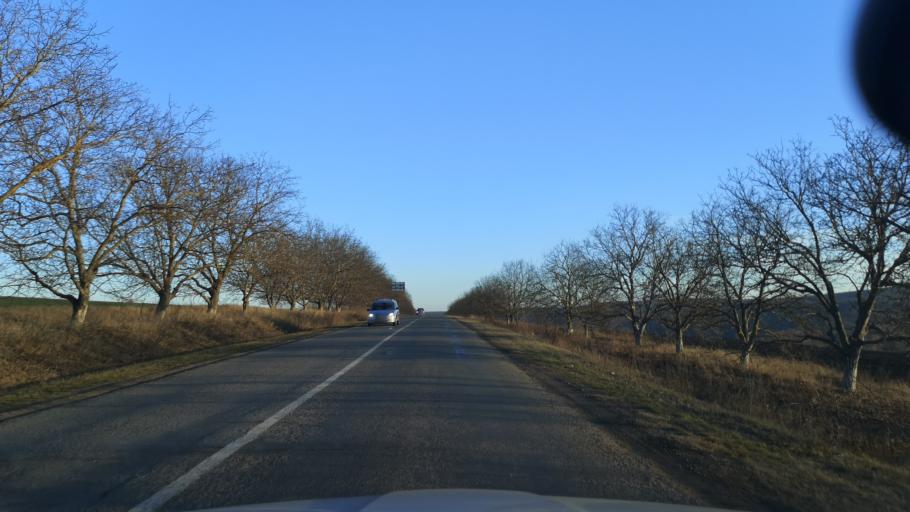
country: MD
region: Orhei
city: Orhei
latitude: 47.2915
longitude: 28.8119
